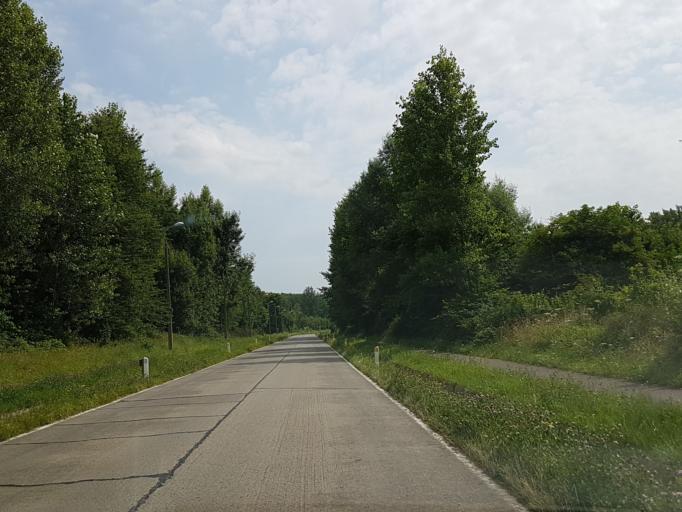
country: BE
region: Flanders
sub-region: Provincie Vlaams-Brabant
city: Herent
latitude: 50.9175
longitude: 4.6375
